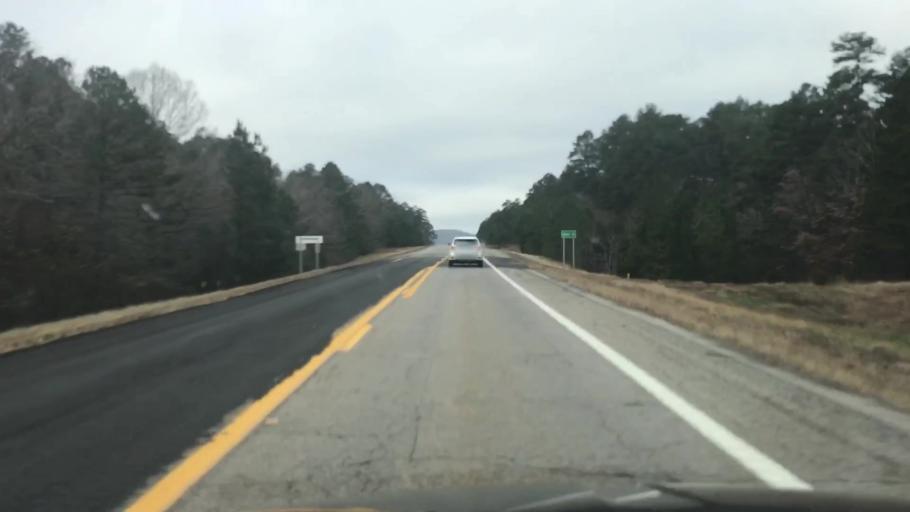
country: US
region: Arkansas
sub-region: Montgomery County
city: Mount Ida
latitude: 34.6873
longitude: -93.8787
